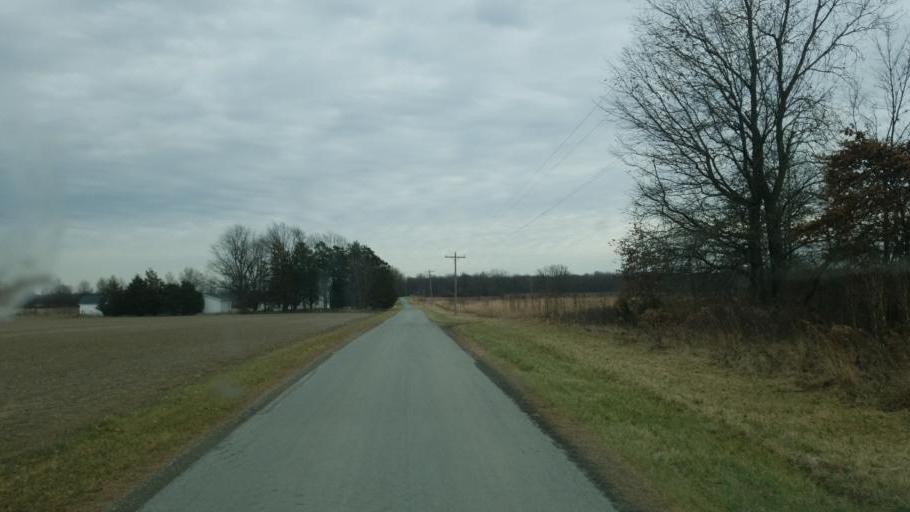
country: US
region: Ohio
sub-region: Wyandot County
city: Upper Sandusky
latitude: 40.7163
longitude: -83.3763
